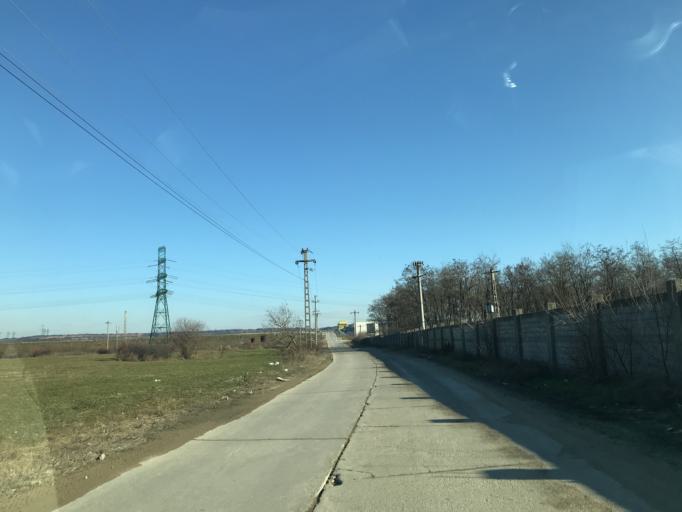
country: RO
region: Olt
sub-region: Comuna Slatioara
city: Slatioara
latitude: 44.3924
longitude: 24.3400
